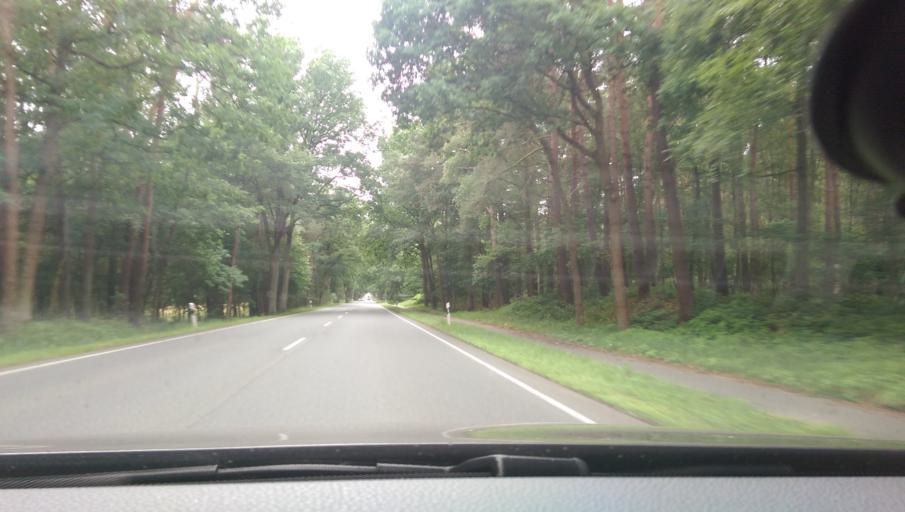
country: DE
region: Lower Saxony
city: Ahausen
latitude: 53.0565
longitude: 9.3392
